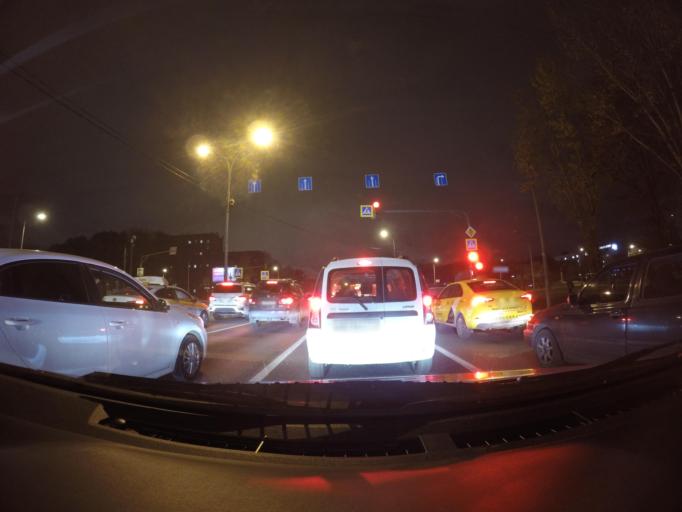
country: RU
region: Moscow
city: Kuz'minki
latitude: 55.6968
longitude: 37.8062
